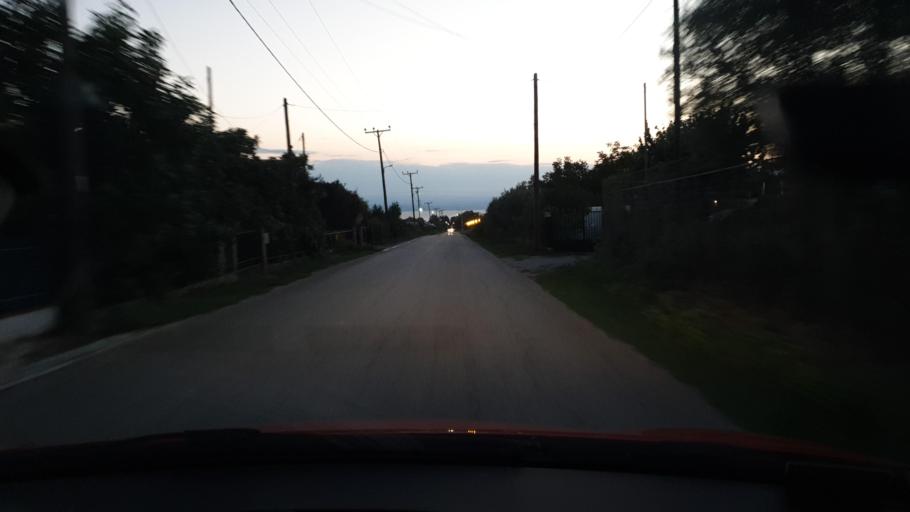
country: GR
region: Central Macedonia
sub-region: Nomos Thessalonikis
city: Agia Triada
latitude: 40.4969
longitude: 22.8413
